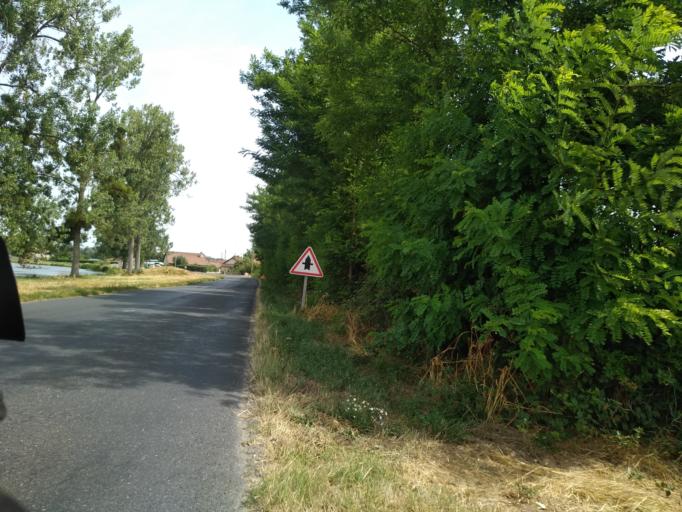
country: FR
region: Bourgogne
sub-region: Departement de Saone-et-Loire
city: Digoin
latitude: 46.4647
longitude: 3.9664
